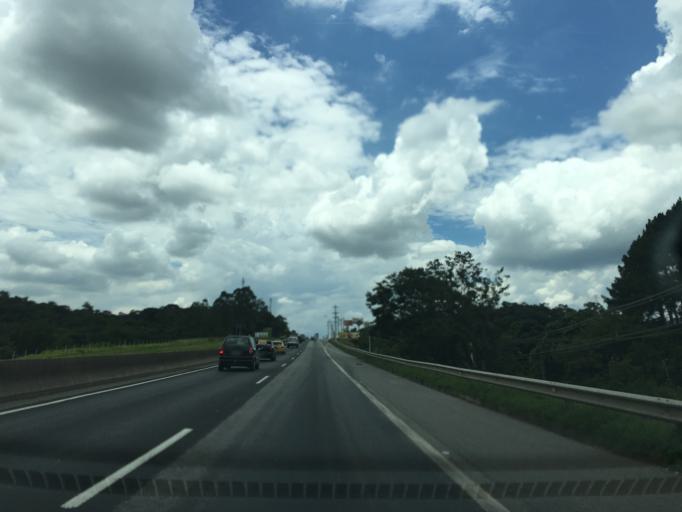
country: BR
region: Sao Paulo
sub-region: Atibaia
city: Atibaia
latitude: -23.2122
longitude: -46.5931
